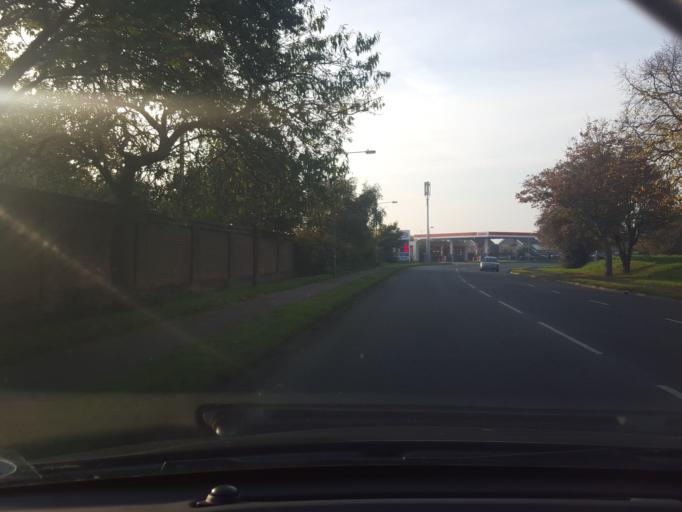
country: GB
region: England
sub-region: Essex
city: Frinton-on-Sea
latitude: 51.8381
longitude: 1.2416
